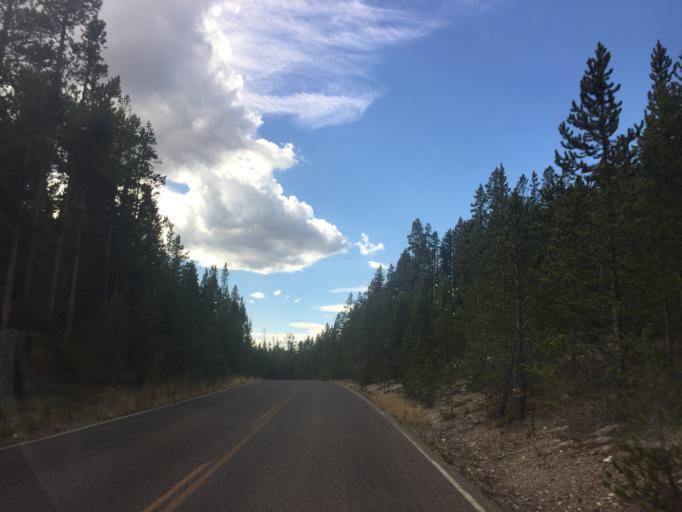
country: US
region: Montana
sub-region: Gallatin County
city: West Yellowstone
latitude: 44.7297
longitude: -110.4768
